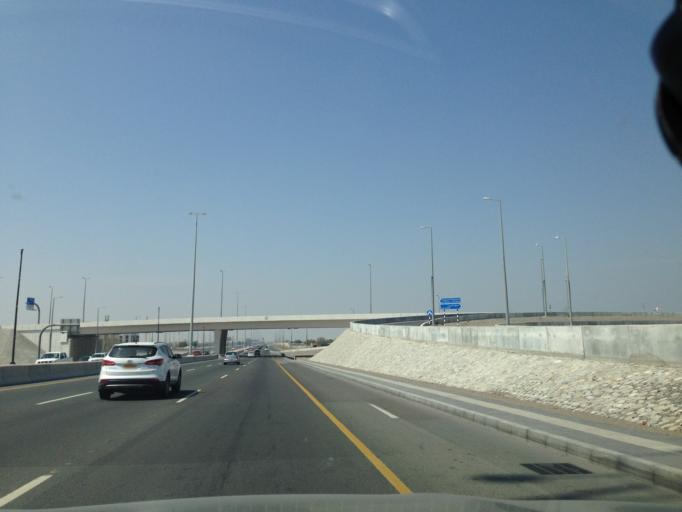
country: OM
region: Muhafazat Masqat
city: As Sib al Jadidah
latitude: 23.6587
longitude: 58.1898
